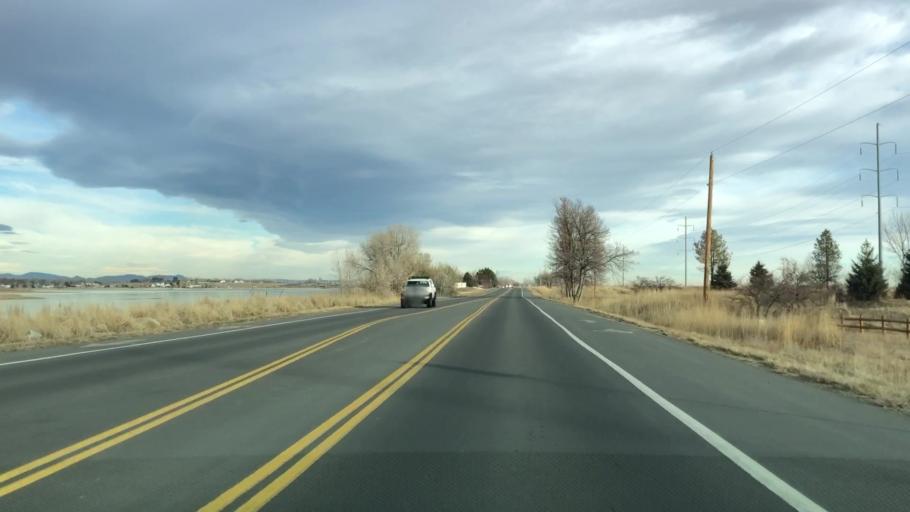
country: US
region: Colorado
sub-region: Larimer County
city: Loveland
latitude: 40.4324
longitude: -105.0454
